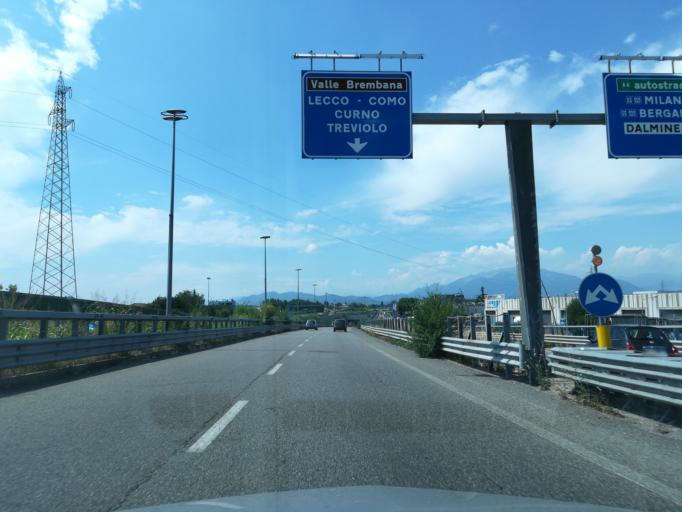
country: IT
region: Lombardy
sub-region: Provincia di Bergamo
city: Lallio
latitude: 45.6480
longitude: 9.6254
